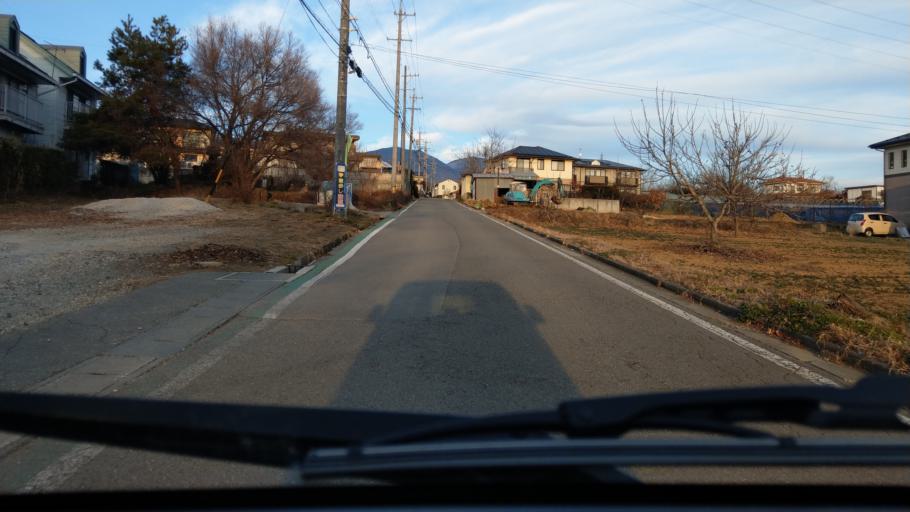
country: JP
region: Nagano
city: Komoro
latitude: 36.3444
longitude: 138.3889
